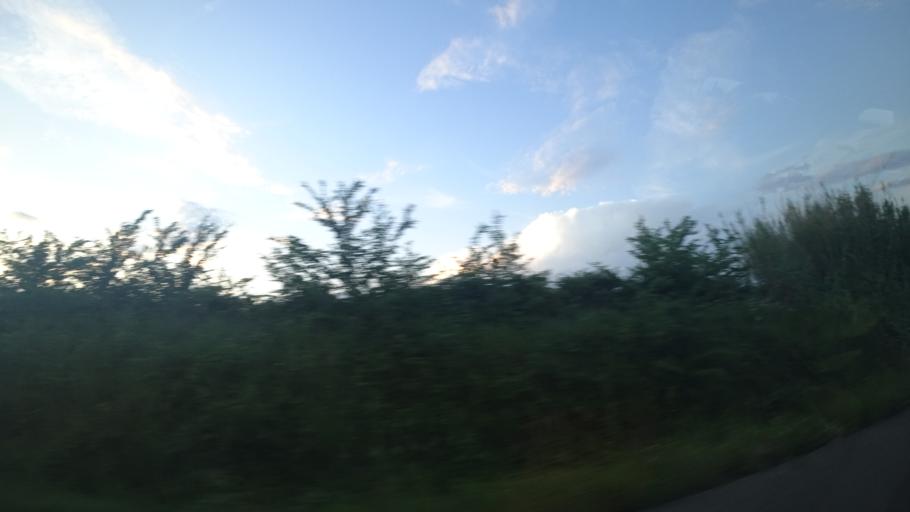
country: FR
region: Languedoc-Roussillon
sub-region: Departement de l'Herault
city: Maraussan
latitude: 43.3351
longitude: 3.1716
